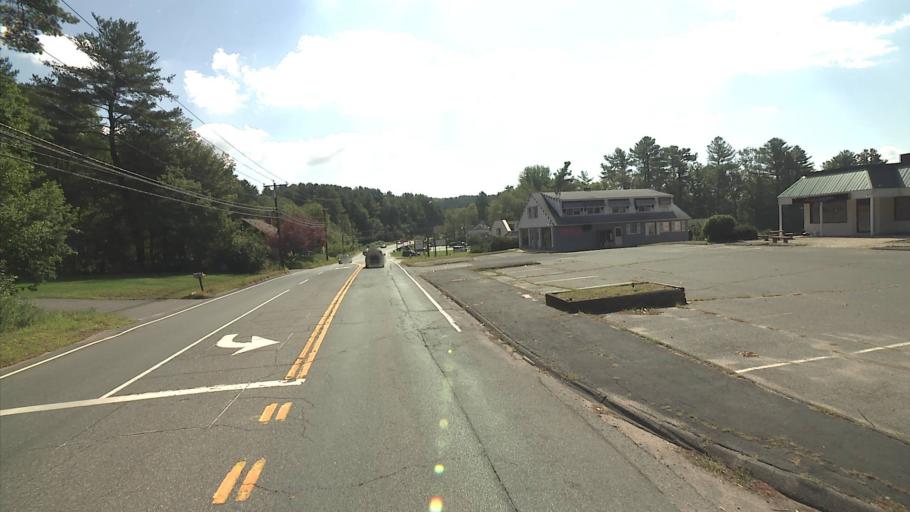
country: US
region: Connecticut
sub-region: Tolland County
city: Stafford Springs
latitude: 41.9647
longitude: -72.3207
